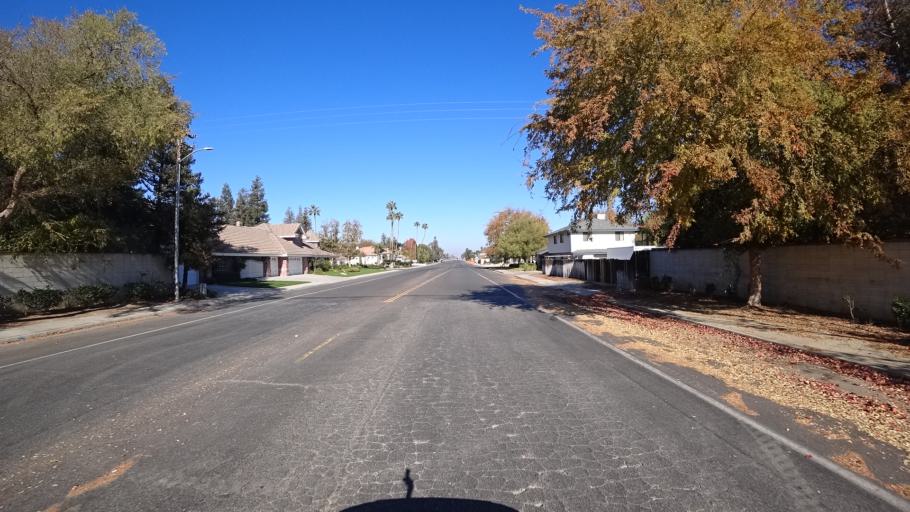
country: US
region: California
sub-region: Kern County
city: Rosedale
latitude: 35.3724
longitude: -119.1368
